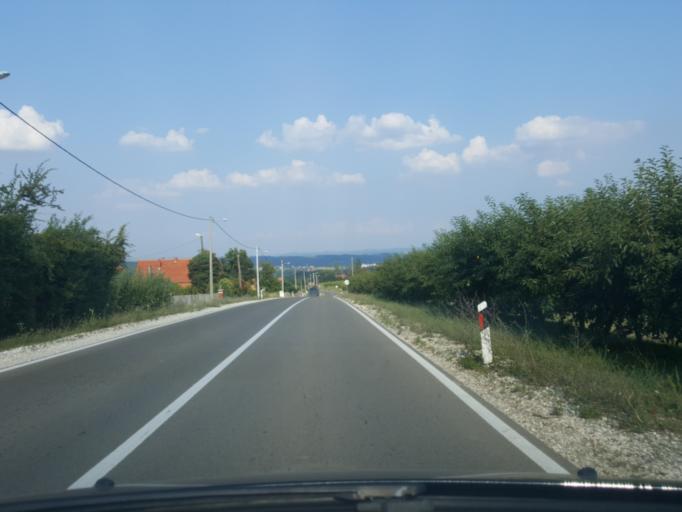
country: RS
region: Central Serbia
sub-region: Sumadijski Okrug
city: Topola
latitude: 44.2276
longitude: 20.6375
